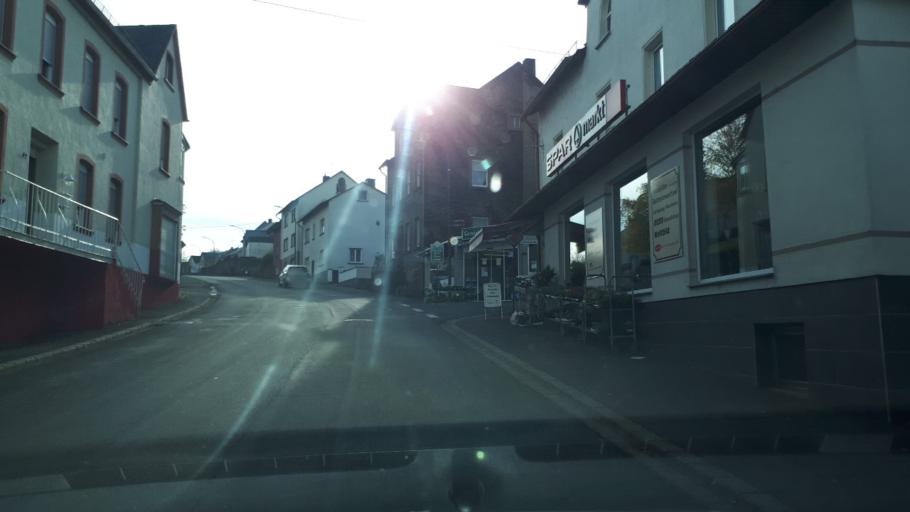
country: DE
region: Rheinland-Pfalz
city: Lutzerath
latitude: 50.1274
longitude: 7.0053
